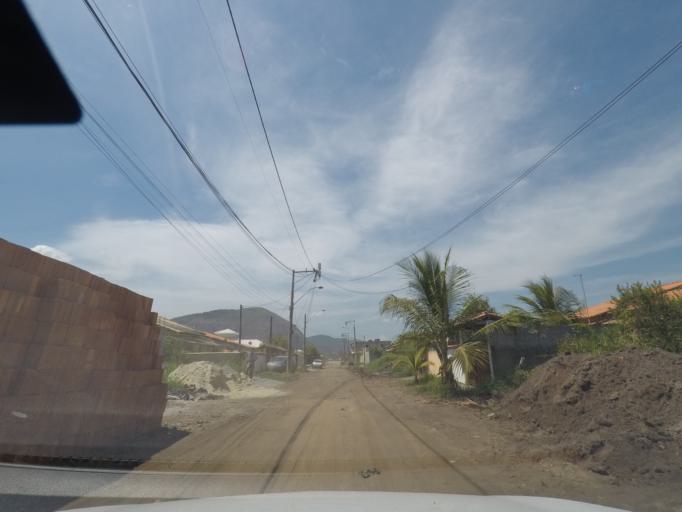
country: BR
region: Rio de Janeiro
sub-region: Marica
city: Marica
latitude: -22.9608
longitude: -42.9559
